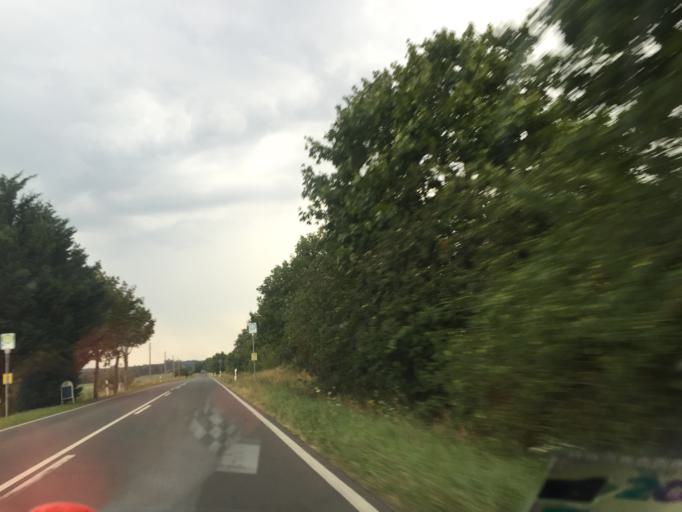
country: DE
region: Brandenburg
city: Zehdenick
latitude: 52.9933
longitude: 13.3037
